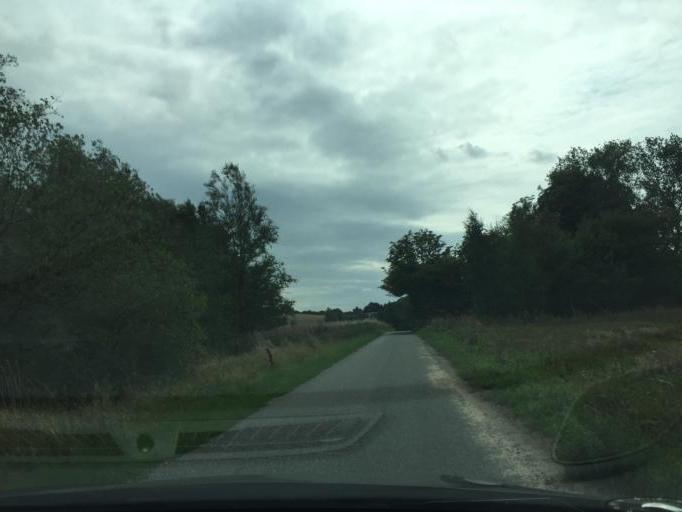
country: DK
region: South Denmark
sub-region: Assens Kommune
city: Vissenbjerg
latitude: 55.3586
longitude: 10.1164
